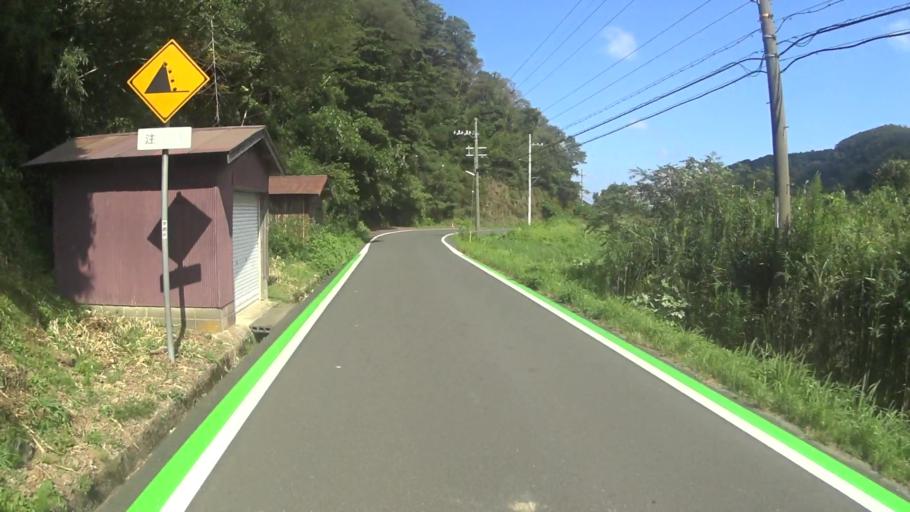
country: JP
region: Kyoto
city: Miyazu
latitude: 35.7308
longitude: 135.2660
